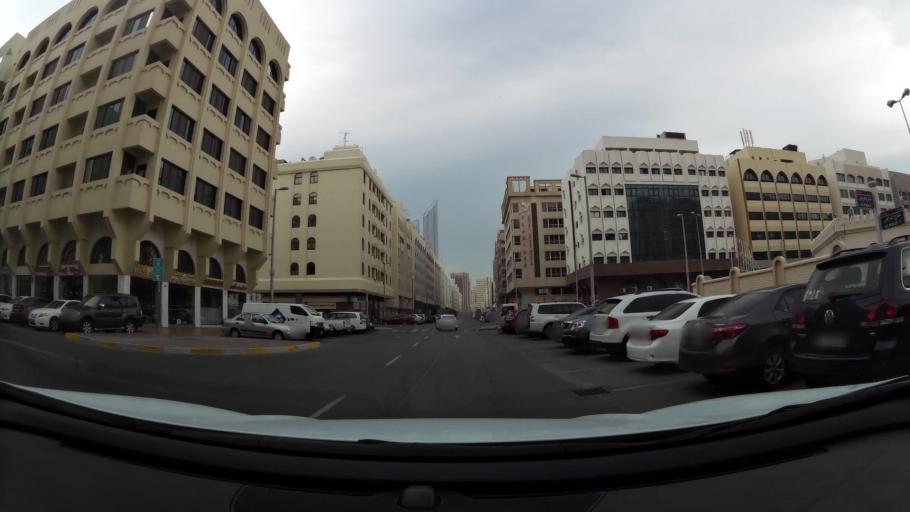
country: AE
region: Abu Dhabi
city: Abu Dhabi
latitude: 24.4789
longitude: 54.3667
